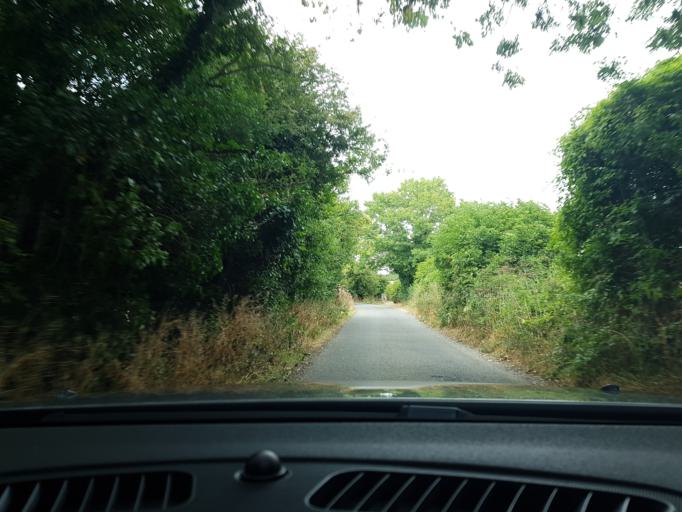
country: GB
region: England
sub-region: West Berkshire
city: Hungerford
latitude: 51.4359
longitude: -1.4778
